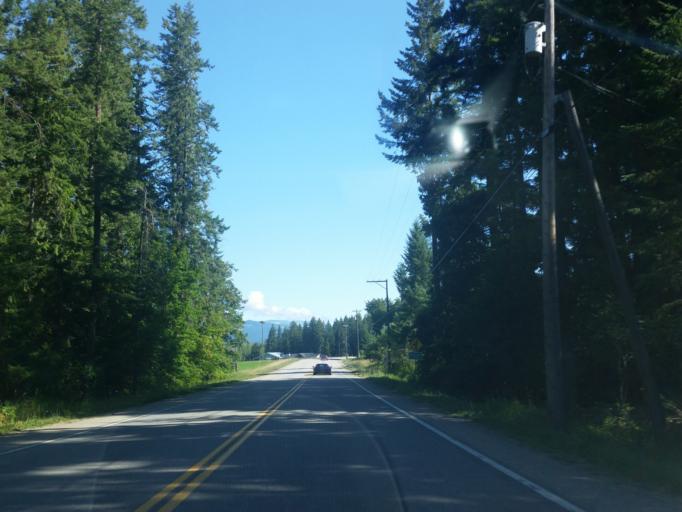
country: CA
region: British Columbia
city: Enderby
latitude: 50.6788
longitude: -119.0545
